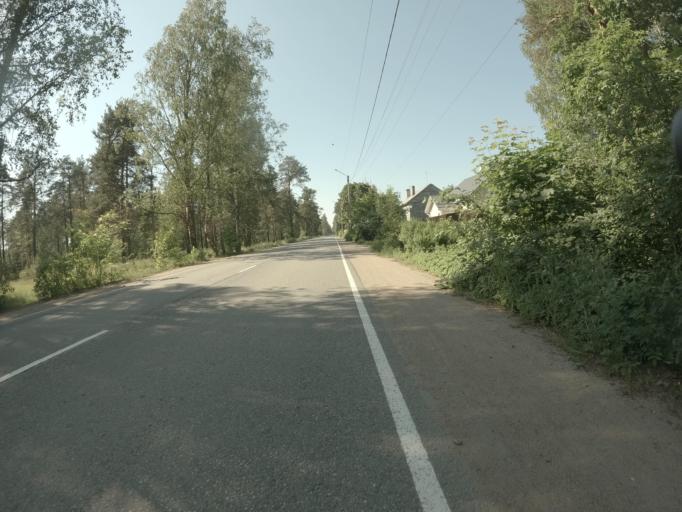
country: RU
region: Leningrad
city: Yakovlevo
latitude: 60.4712
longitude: 29.2829
